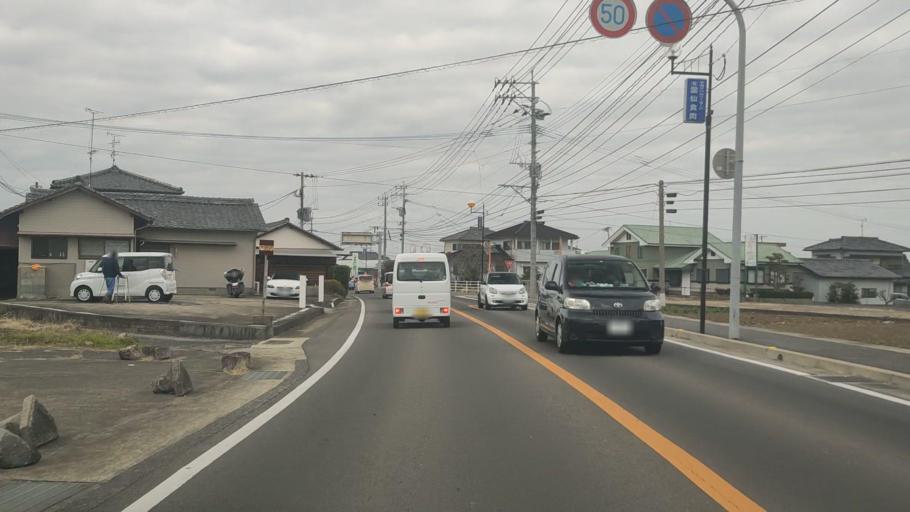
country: JP
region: Nagasaki
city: Shimabara
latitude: 32.8554
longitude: 130.3379
